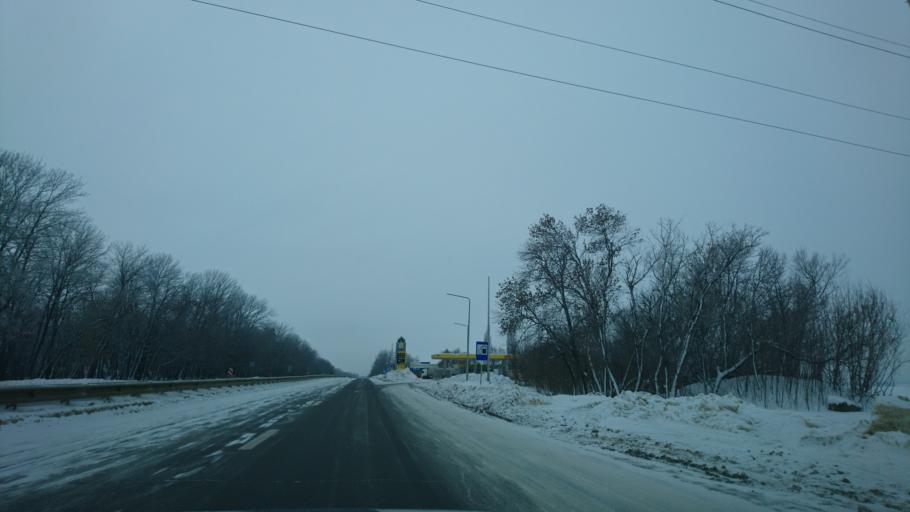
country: RU
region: Belgorod
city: Mayskiy
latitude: 50.4363
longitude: 36.3902
